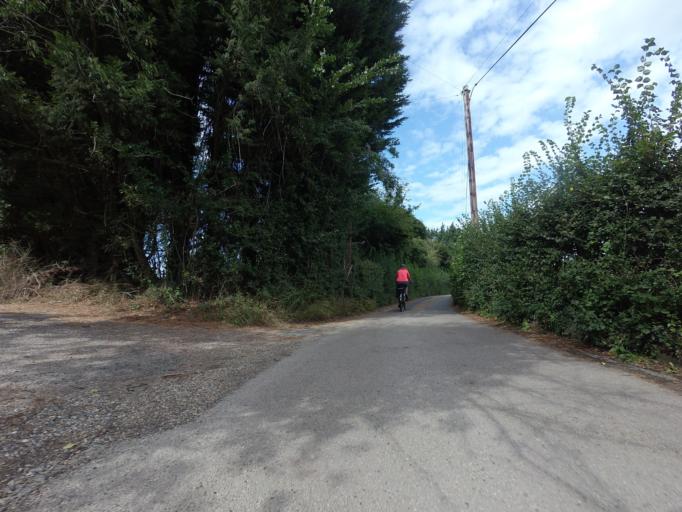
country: GB
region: England
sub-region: Kent
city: Shoreham
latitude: 51.3064
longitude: 0.1794
